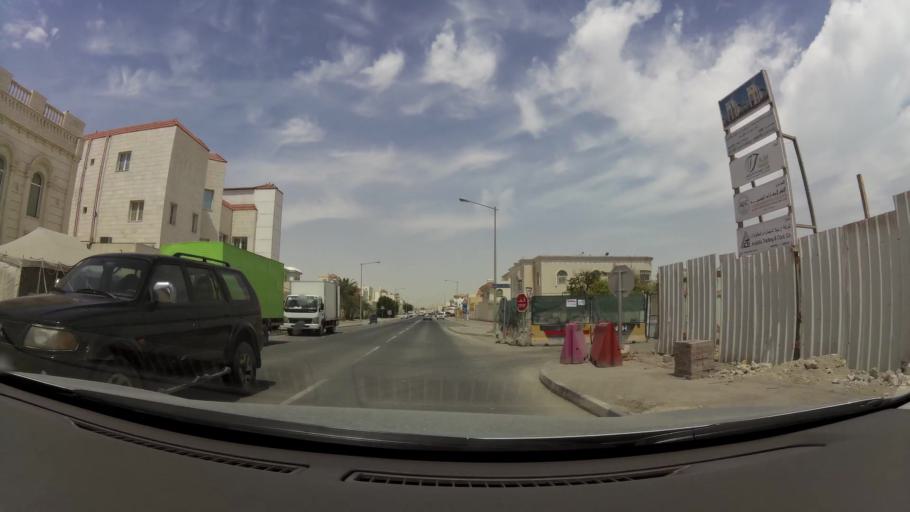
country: QA
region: Baladiyat ar Rayyan
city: Ar Rayyan
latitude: 25.2649
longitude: 51.4264
